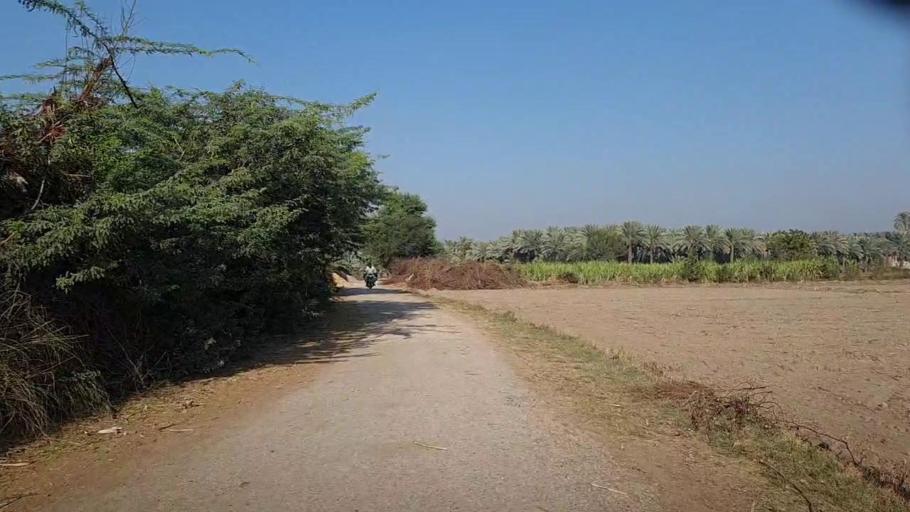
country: PK
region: Sindh
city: Ranipur
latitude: 27.2535
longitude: 68.5507
